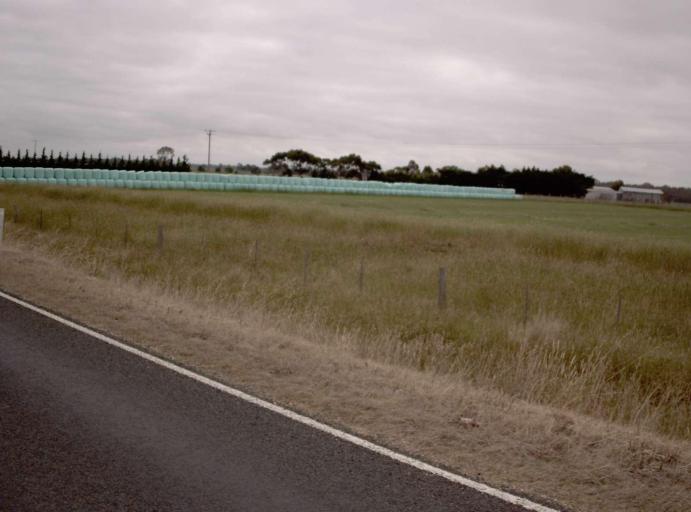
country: AU
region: Victoria
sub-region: Wellington
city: Sale
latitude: -38.0780
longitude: 146.9882
